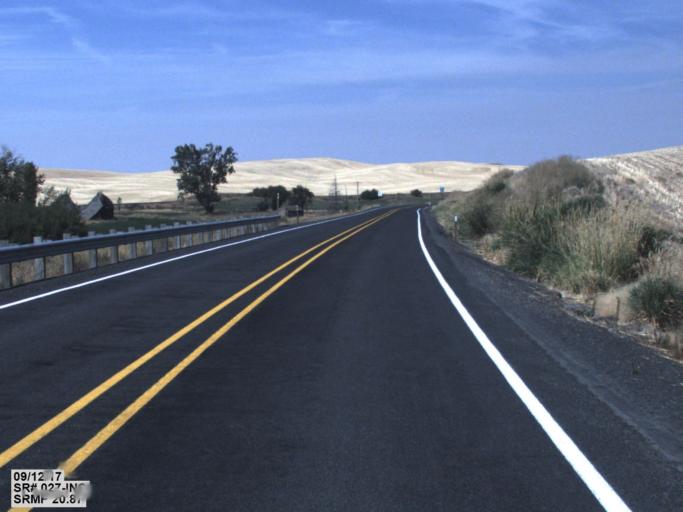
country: US
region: Washington
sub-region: Whitman County
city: Pullman
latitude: 46.9682
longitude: -117.1156
